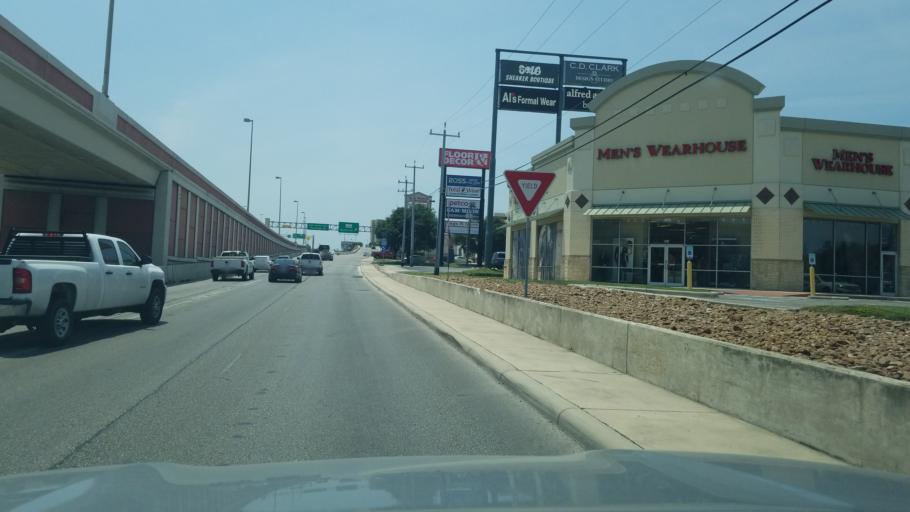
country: US
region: Texas
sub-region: Bexar County
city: Castle Hills
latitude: 29.5209
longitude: -98.4952
